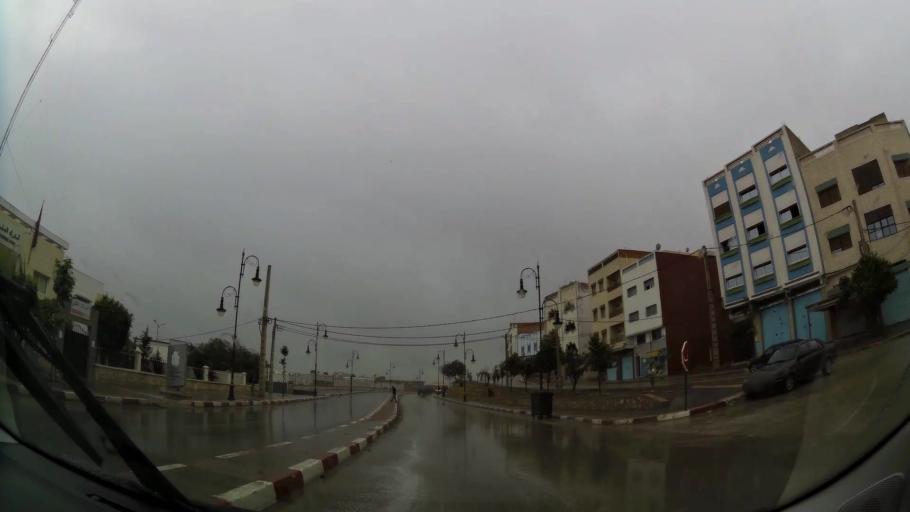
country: MA
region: Taza-Al Hoceima-Taounate
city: Imzourene
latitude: 35.1503
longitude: -3.8448
